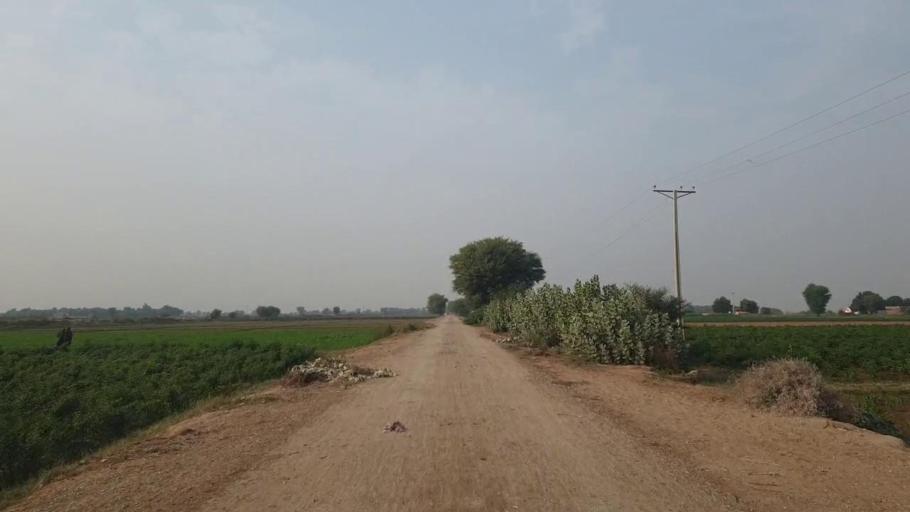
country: PK
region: Sindh
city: Sann
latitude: 26.0601
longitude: 68.1220
